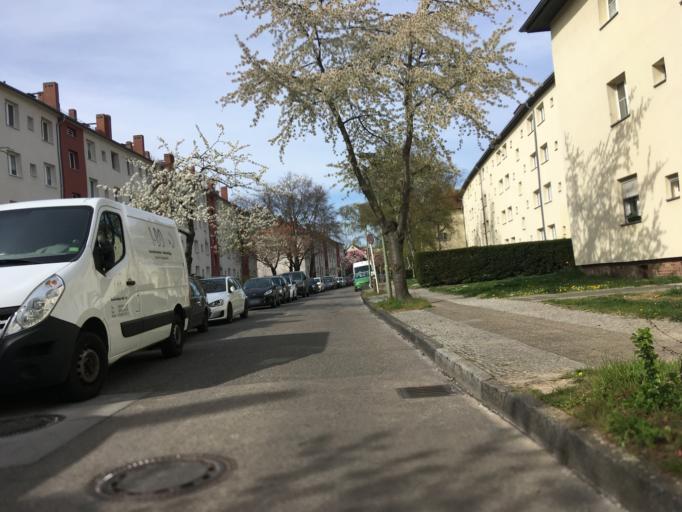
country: DE
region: Berlin
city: Mariendorf
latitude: 52.4441
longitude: 13.3896
